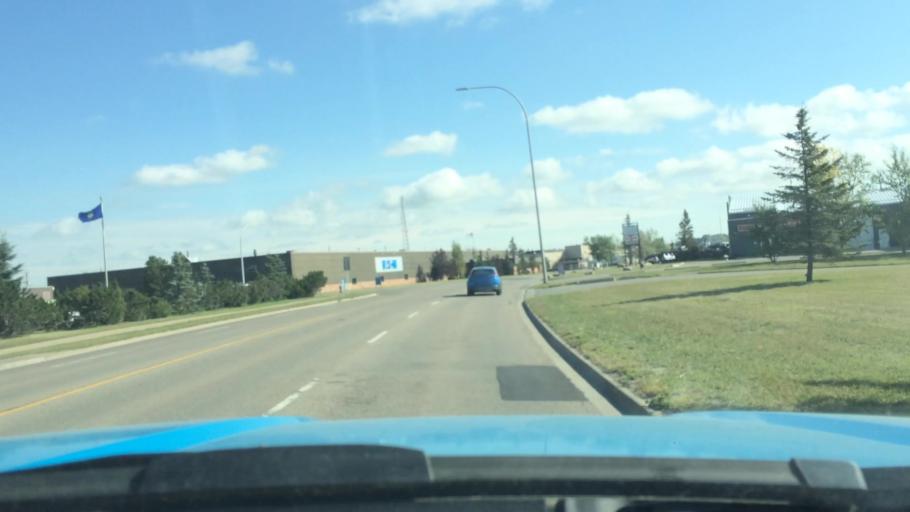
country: CA
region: Alberta
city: Airdrie
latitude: 51.2880
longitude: -113.9951
